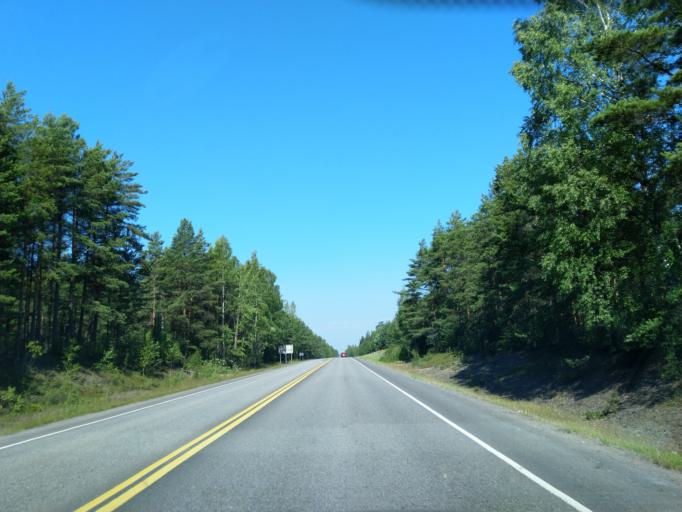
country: FI
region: Satakunta
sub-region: Pori
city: Harjavalta
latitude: 61.2973
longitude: 22.1530
